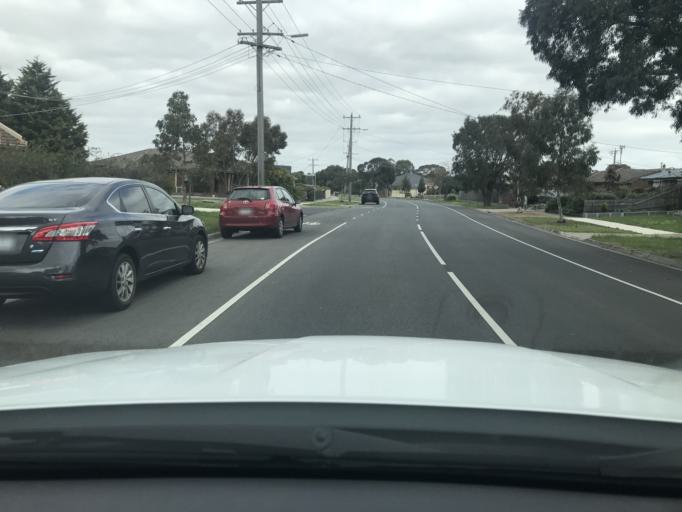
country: AU
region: Victoria
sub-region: Hume
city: Craigieburn
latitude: -37.5955
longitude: 144.9261
